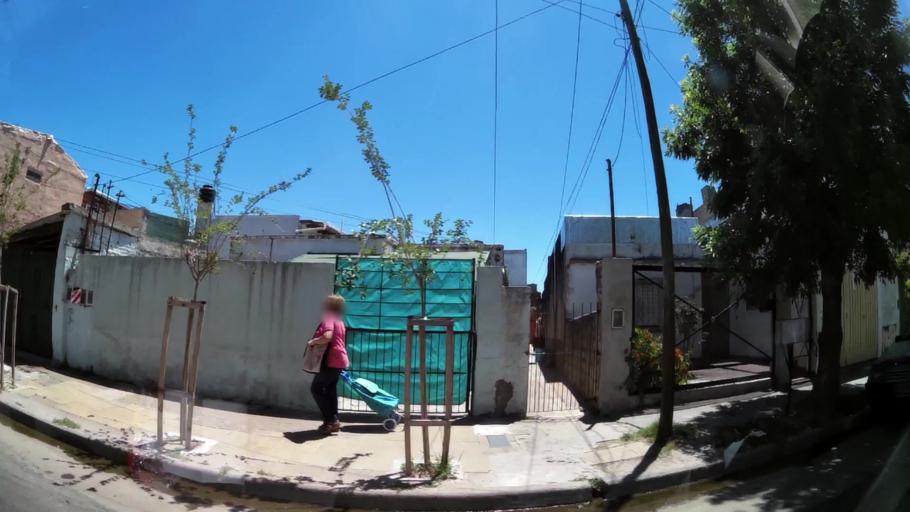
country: AR
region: Buenos Aires
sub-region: Partido de Tigre
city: Tigre
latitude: -34.4492
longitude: -58.5582
